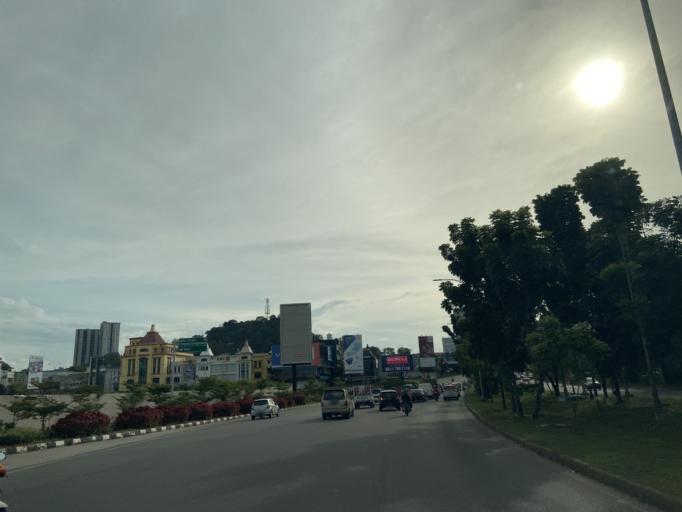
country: SG
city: Singapore
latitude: 1.1303
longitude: 104.0168
